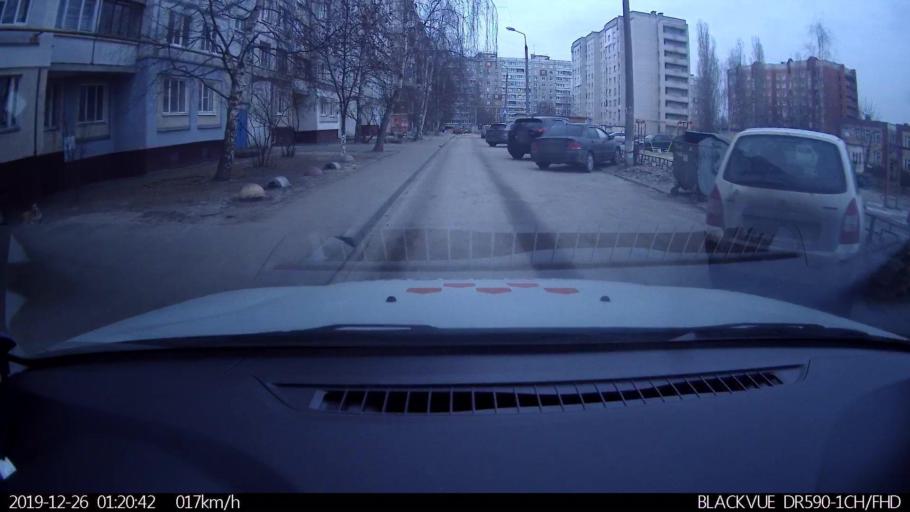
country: RU
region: Nizjnij Novgorod
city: Nizhniy Novgorod
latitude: 56.2730
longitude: 43.8855
